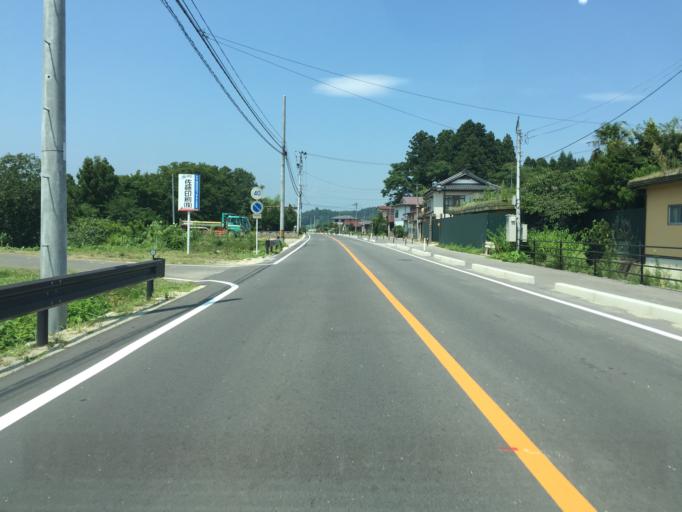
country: JP
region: Miyagi
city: Marumori
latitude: 37.8837
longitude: 140.8190
